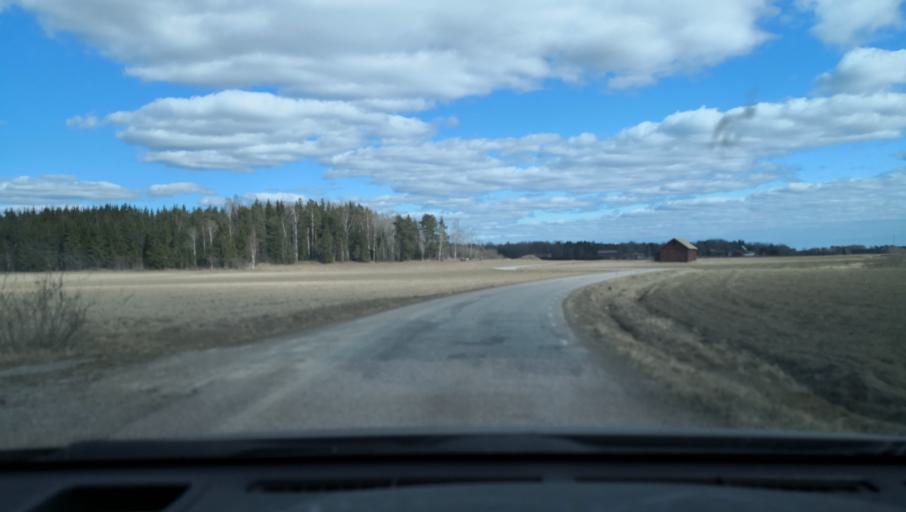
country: SE
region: Vaestmanland
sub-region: Sala Kommun
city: Sala
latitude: 59.8618
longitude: 16.5830
